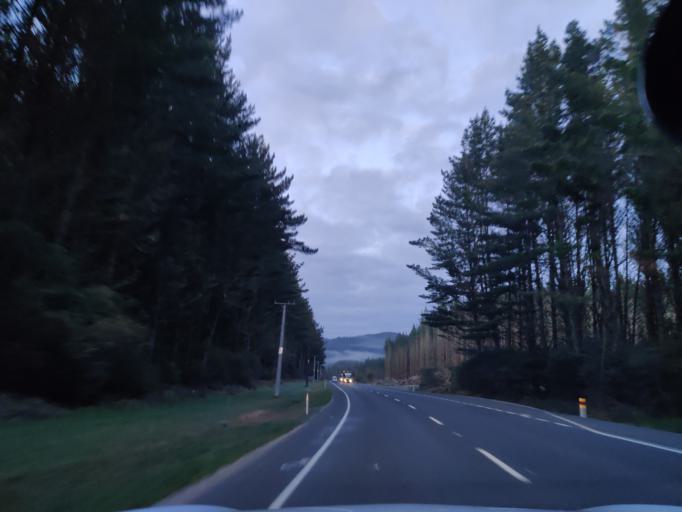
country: NZ
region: Waikato
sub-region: South Waikato District
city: Tokoroa
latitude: -38.3678
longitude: 176.0023
